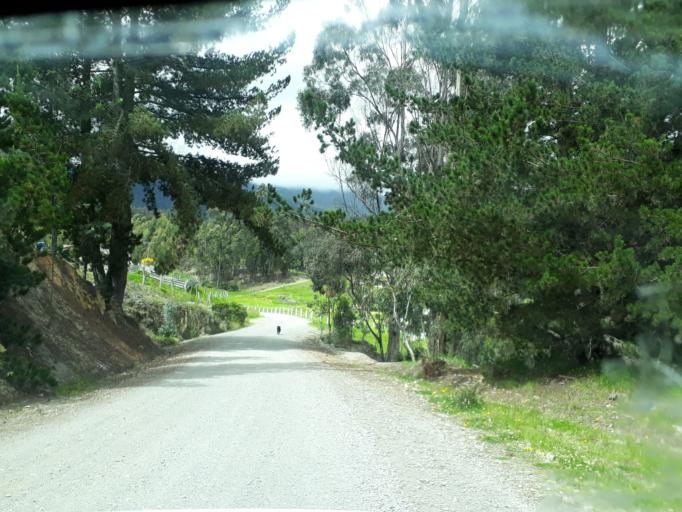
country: CO
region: Cundinamarca
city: La Mesa
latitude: 5.2824
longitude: -73.9088
